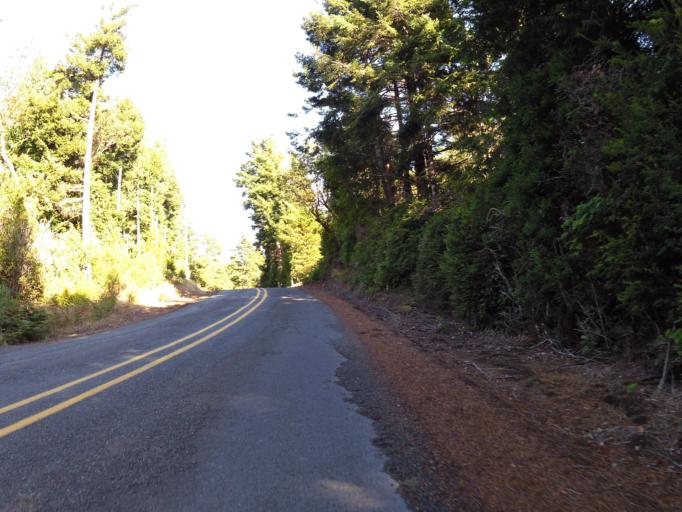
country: US
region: Oregon
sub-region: Coos County
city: Bandon
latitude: 43.0392
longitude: -124.4006
